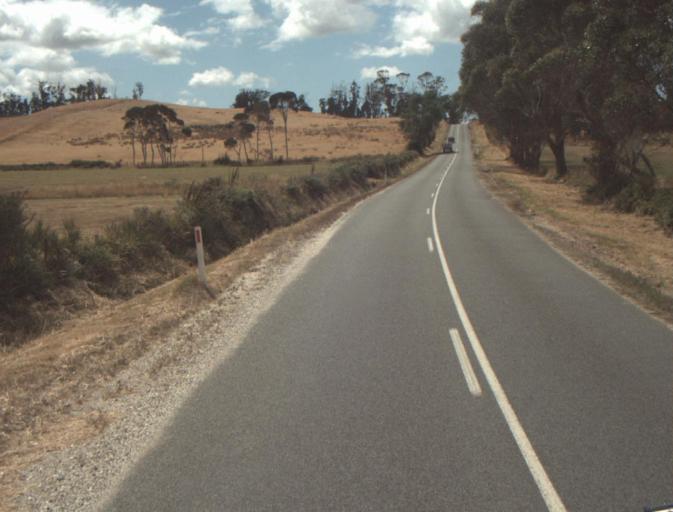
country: AU
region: Tasmania
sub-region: Launceston
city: Mayfield
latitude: -41.2235
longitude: 147.1218
